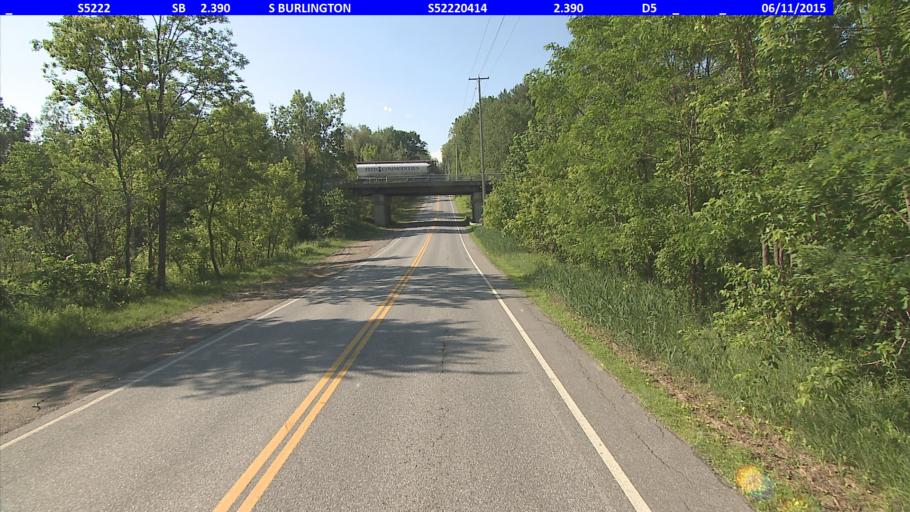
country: US
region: Vermont
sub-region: Chittenden County
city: South Burlington
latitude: 44.4507
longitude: -73.1885
